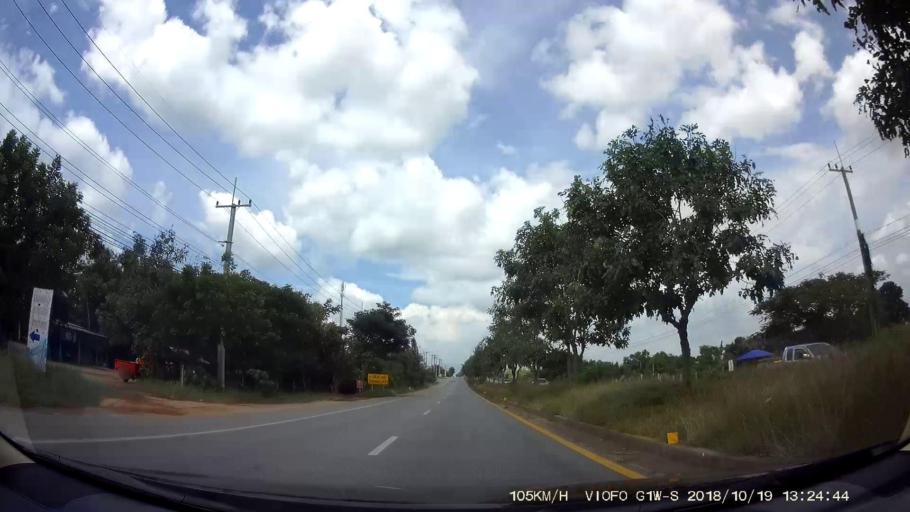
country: TH
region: Chaiyaphum
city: Chatturat
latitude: 15.5112
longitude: 101.8228
